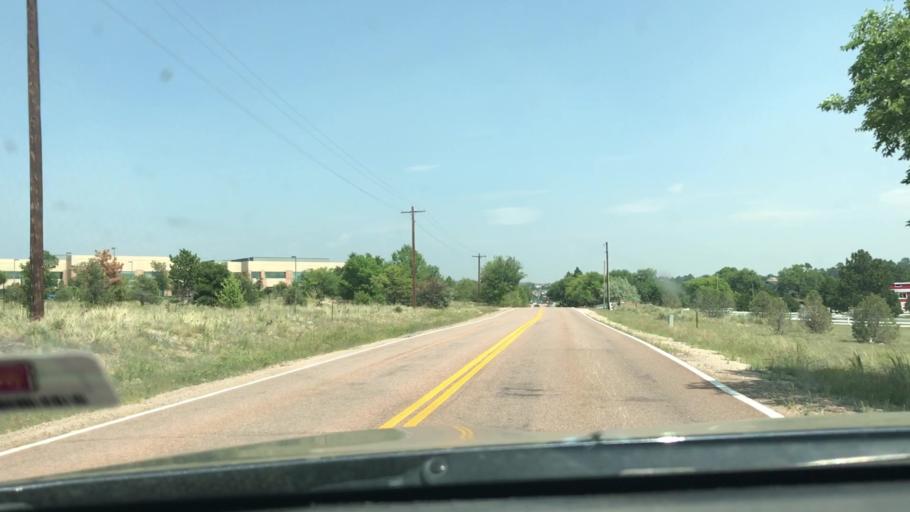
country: US
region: Colorado
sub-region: El Paso County
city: Air Force Academy
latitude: 38.9804
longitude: -104.7952
